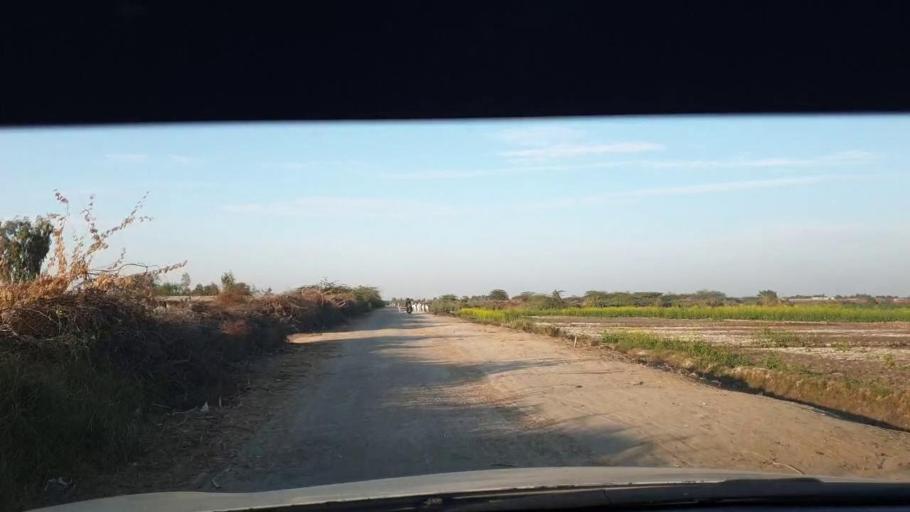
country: PK
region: Sindh
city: Berani
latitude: 25.8057
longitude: 68.8823
